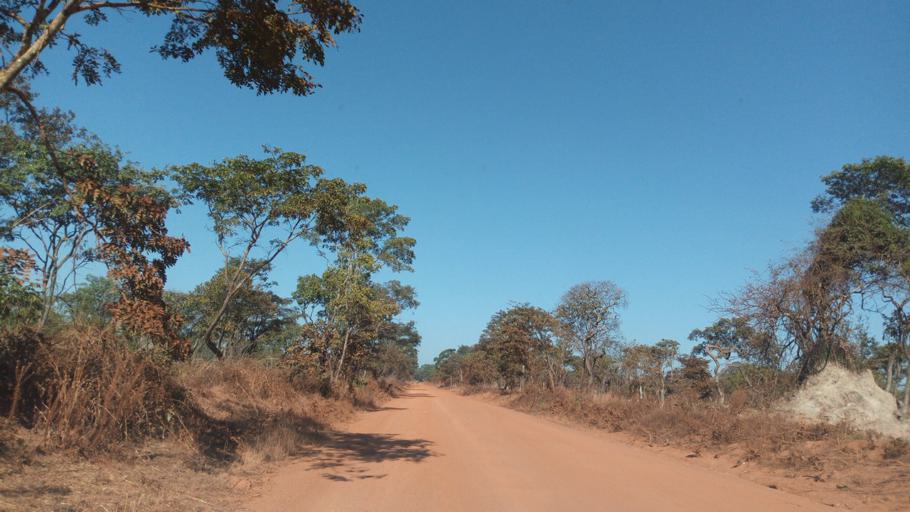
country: ZM
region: Luapula
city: Mwense
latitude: -10.6769
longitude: 28.4058
